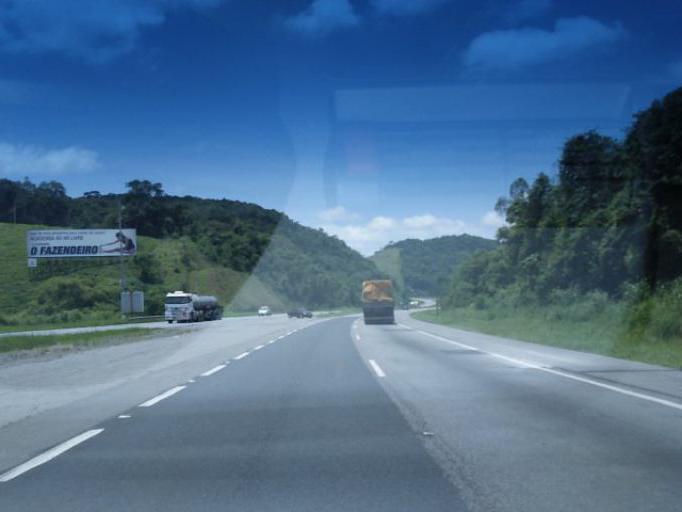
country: BR
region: Sao Paulo
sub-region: Miracatu
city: Miracatu
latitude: -24.2200
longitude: -47.3655
